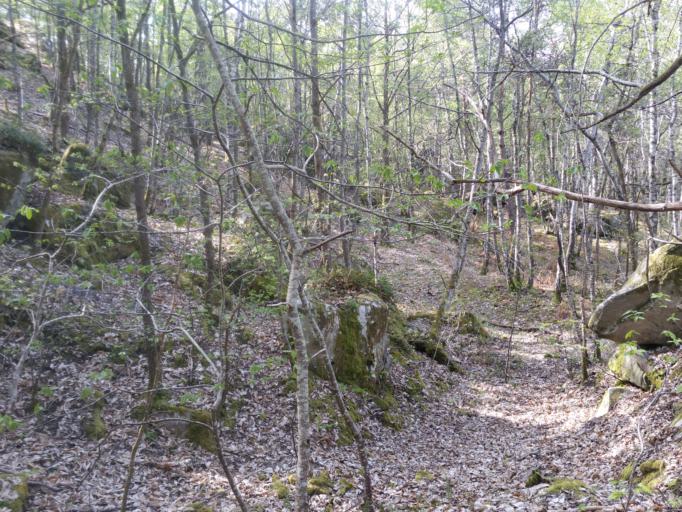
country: FR
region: Ile-de-France
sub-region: Departement de Seine-et-Marne
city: Arbonne-la-Foret
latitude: 48.3950
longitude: 2.5471
